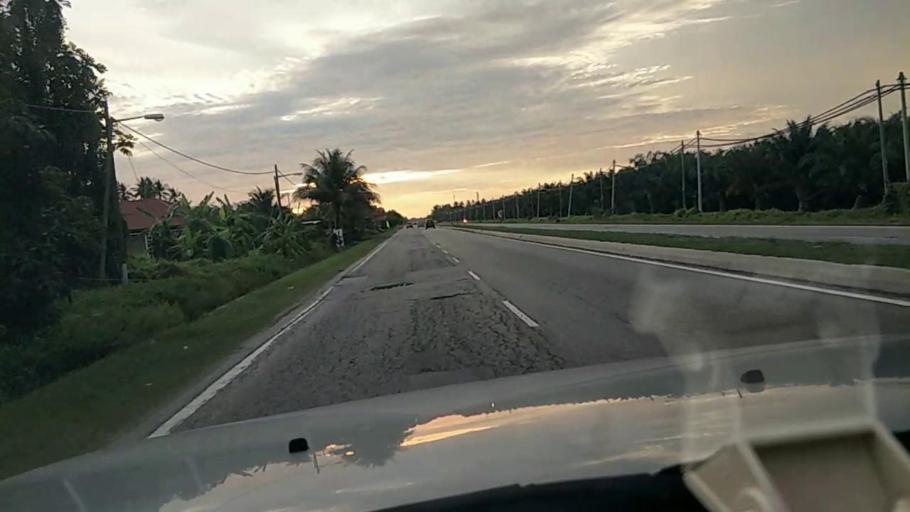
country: MY
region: Perak
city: Kampong Dungun
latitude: 3.1420
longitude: 101.3610
